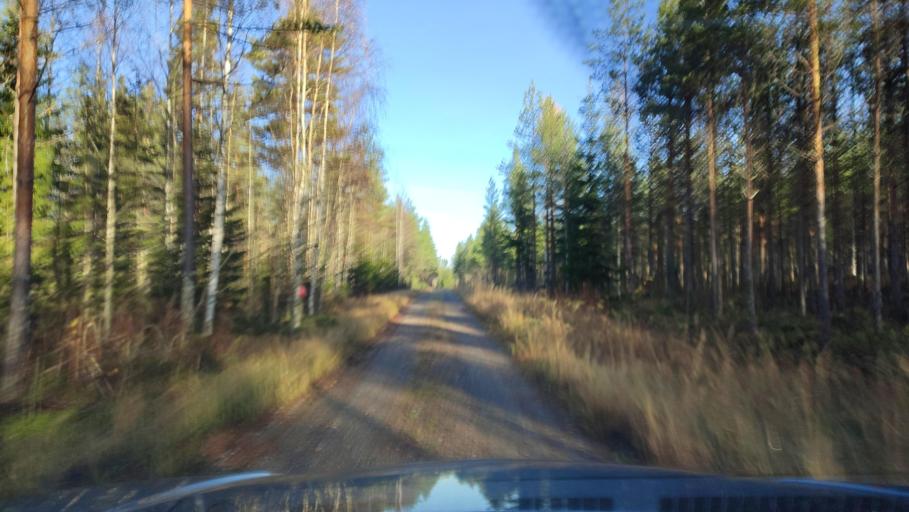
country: FI
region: Southern Ostrobothnia
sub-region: Suupohja
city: Karijoki
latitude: 62.1908
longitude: 21.6070
